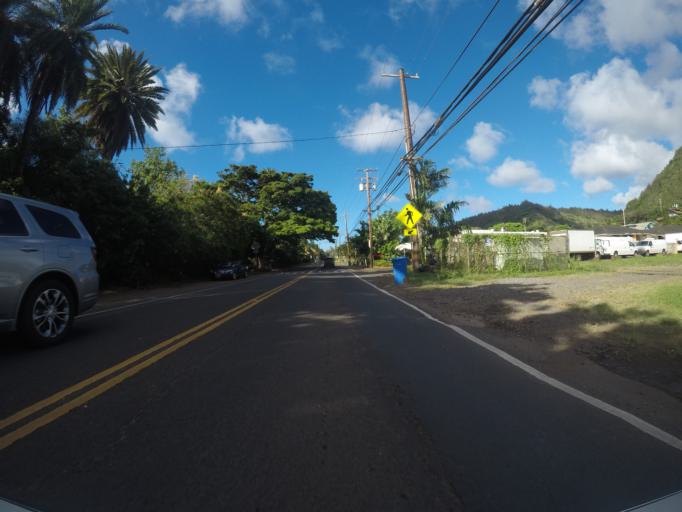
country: US
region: Hawaii
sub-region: Honolulu County
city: Pupukea
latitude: 21.6776
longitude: -158.0371
